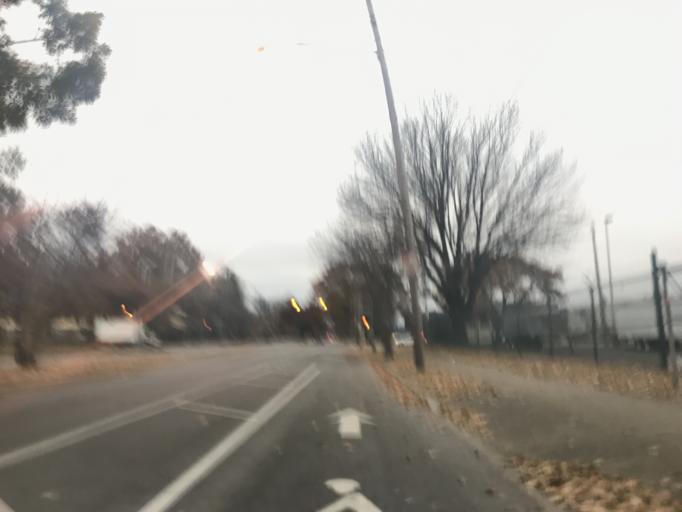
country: US
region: Kentucky
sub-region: Jefferson County
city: Louisville
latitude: 38.2562
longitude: -85.7720
